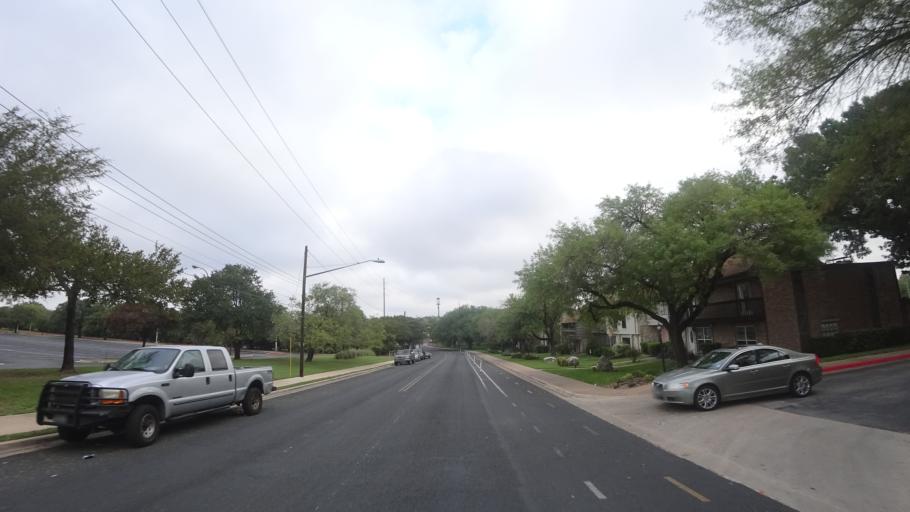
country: US
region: Texas
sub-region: Travis County
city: Wells Branch
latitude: 30.3524
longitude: -97.6868
